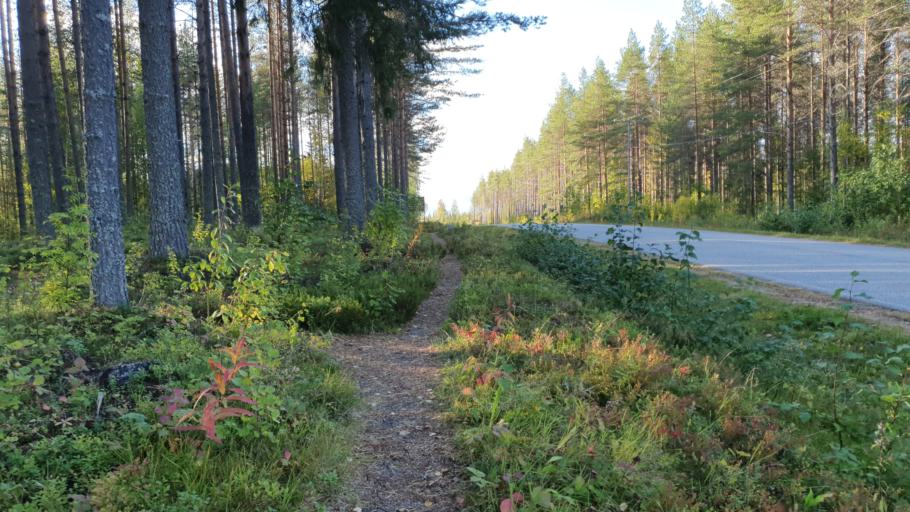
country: FI
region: Kainuu
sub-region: Kehys-Kainuu
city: Kuhmo
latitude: 63.9309
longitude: 29.9729
